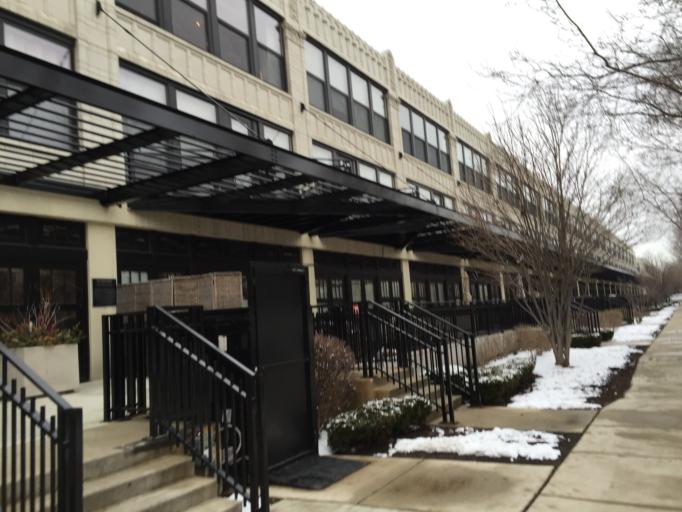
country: US
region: Illinois
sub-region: Cook County
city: Chicago
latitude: 41.8617
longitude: -87.6562
